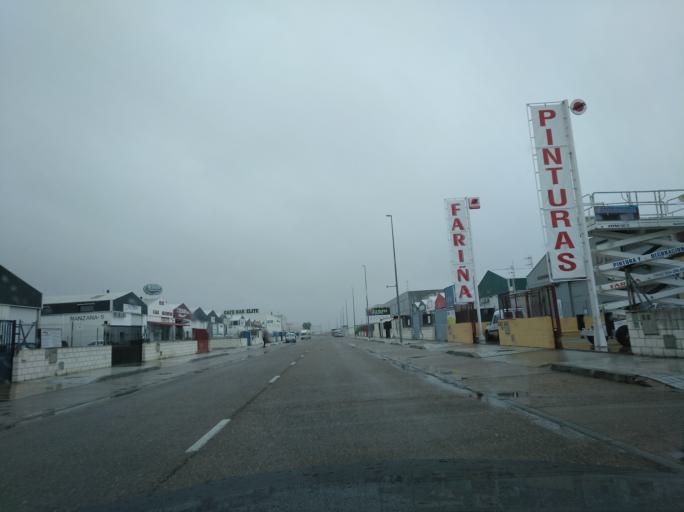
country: ES
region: Extremadura
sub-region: Provincia de Badajoz
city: Badajoz
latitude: 38.9006
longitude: -6.9946
